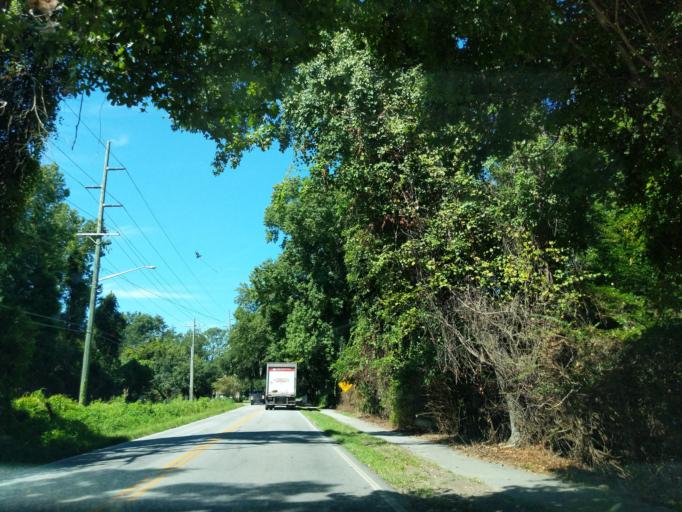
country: US
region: South Carolina
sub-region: Charleston County
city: Charleston
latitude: 32.7252
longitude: -79.9439
